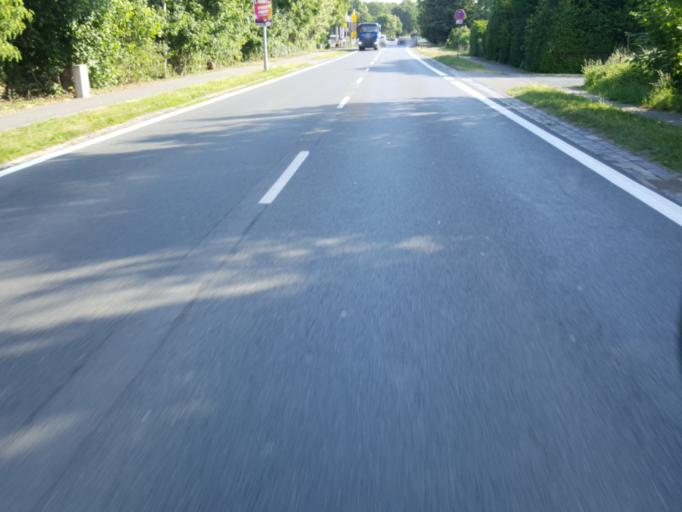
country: DE
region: Lower Saxony
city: Estorf
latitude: 52.5980
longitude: 9.1546
